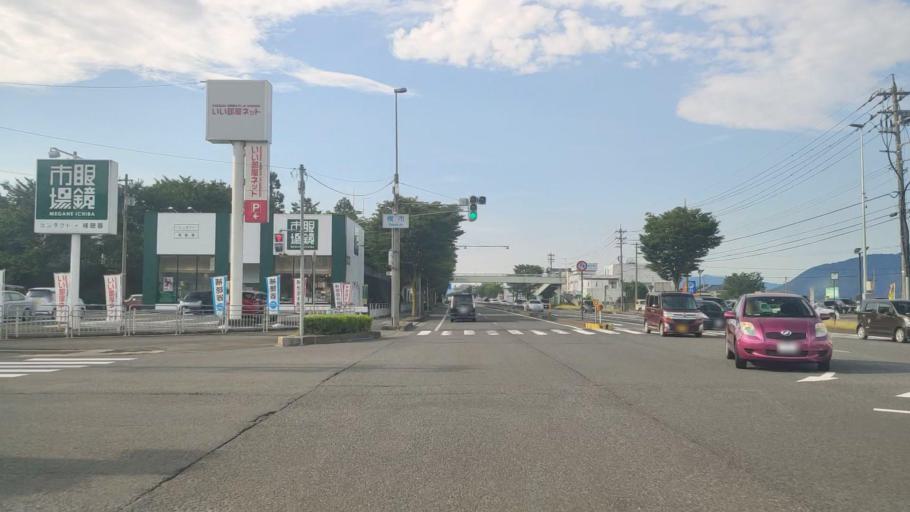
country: JP
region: Fukui
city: Takefu
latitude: 35.9080
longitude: 136.1920
